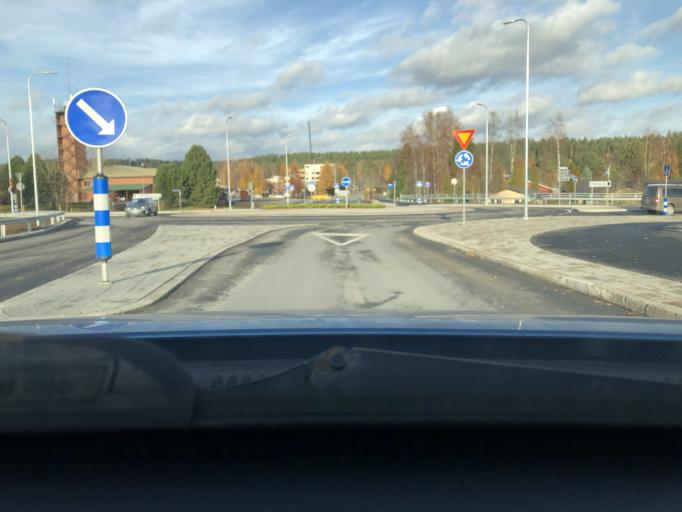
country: FI
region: Pirkanmaa
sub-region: Tampere
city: Kangasala
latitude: 61.4649
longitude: 24.0377
